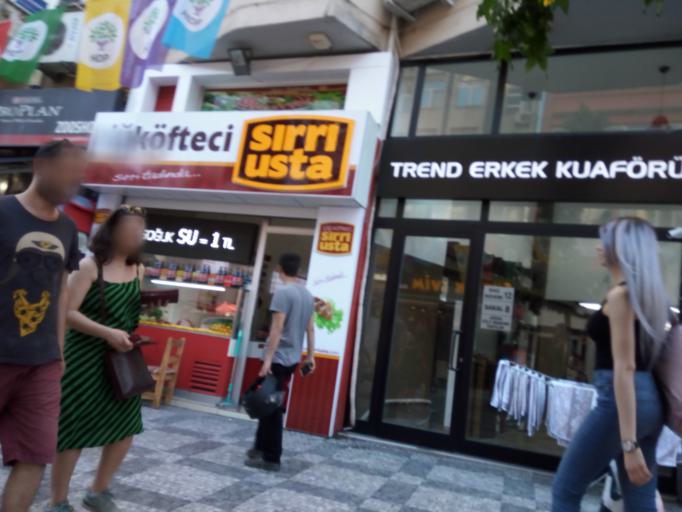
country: TR
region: Istanbul
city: UEskuedar
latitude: 40.9924
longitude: 29.0293
